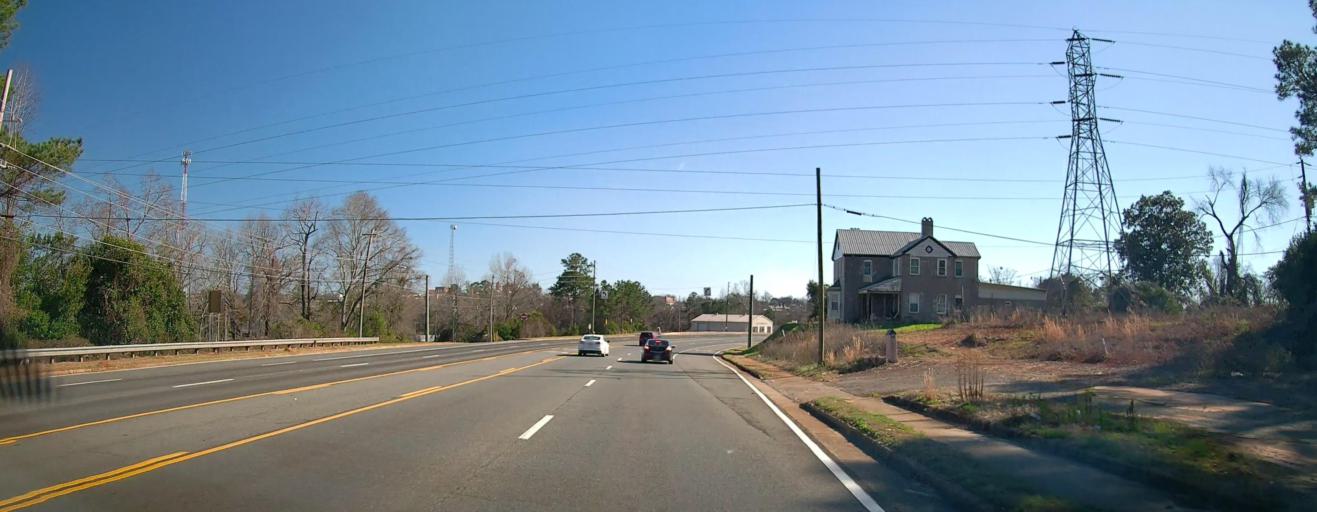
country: US
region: Georgia
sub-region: Sumter County
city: Americus
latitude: 32.0808
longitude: -84.2388
